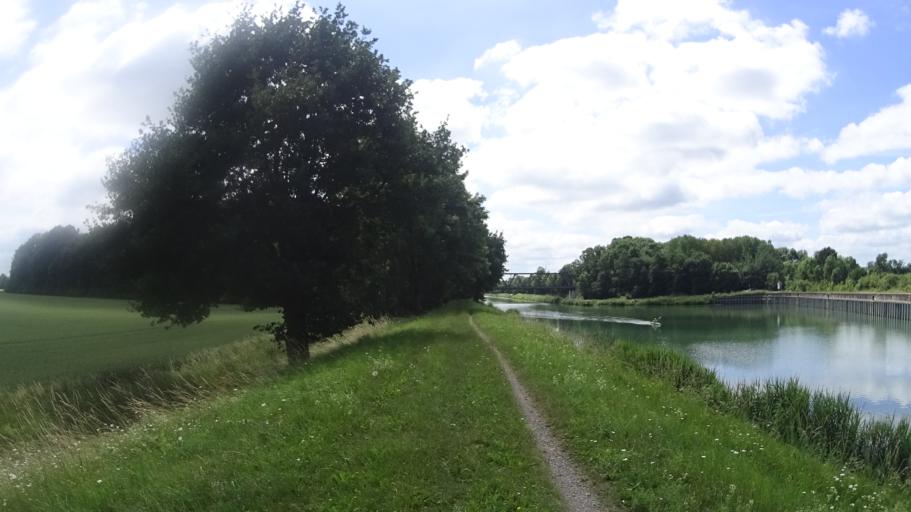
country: DE
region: Lower Saxony
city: Harsum
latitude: 52.2258
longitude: 9.9407
